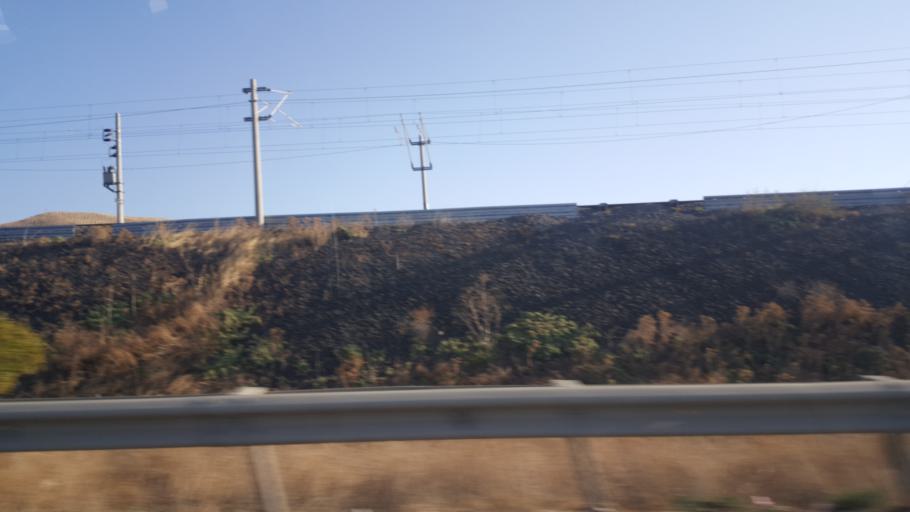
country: TR
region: Ankara
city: Polatli
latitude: 39.5741
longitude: 32.0497
